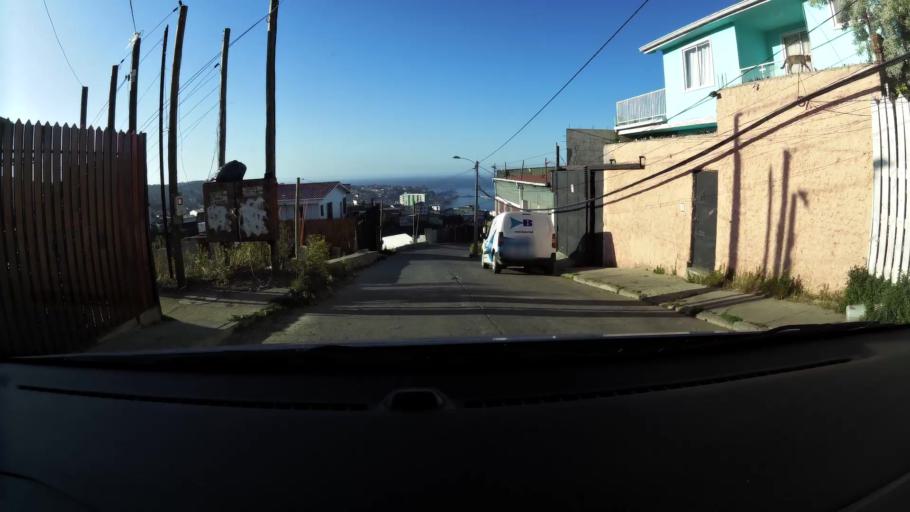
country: CL
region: Valparaiso
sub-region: Provincia de Valparaiso
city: Valparaiso
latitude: -33.0583
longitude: -71.6157
